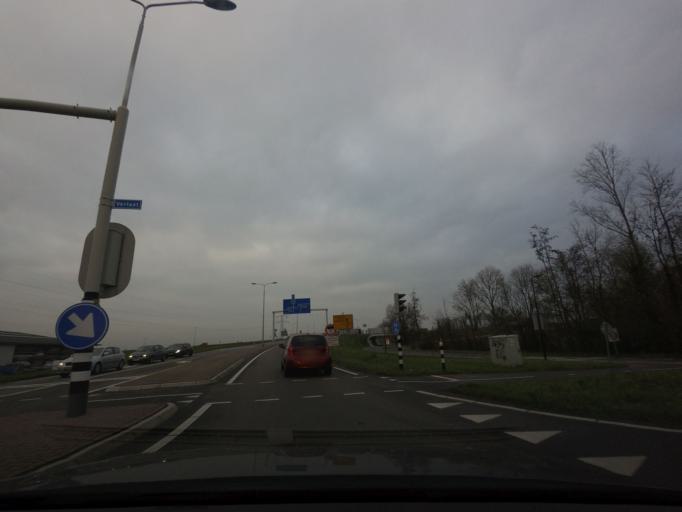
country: NL
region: North Holland
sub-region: Gemeente Heerhugowaard
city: Heerhugowaard
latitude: 52.7209
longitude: 4.8574
